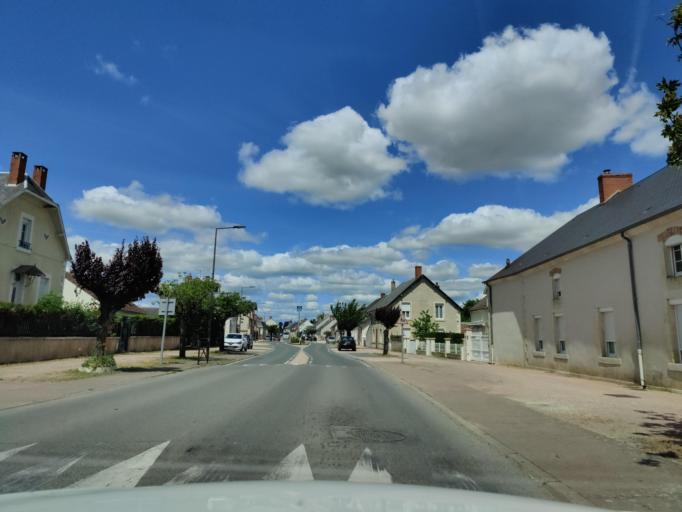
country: FR
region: Centre
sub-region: Departement du Cher
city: Levet
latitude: 46.9231
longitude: 2.4098
